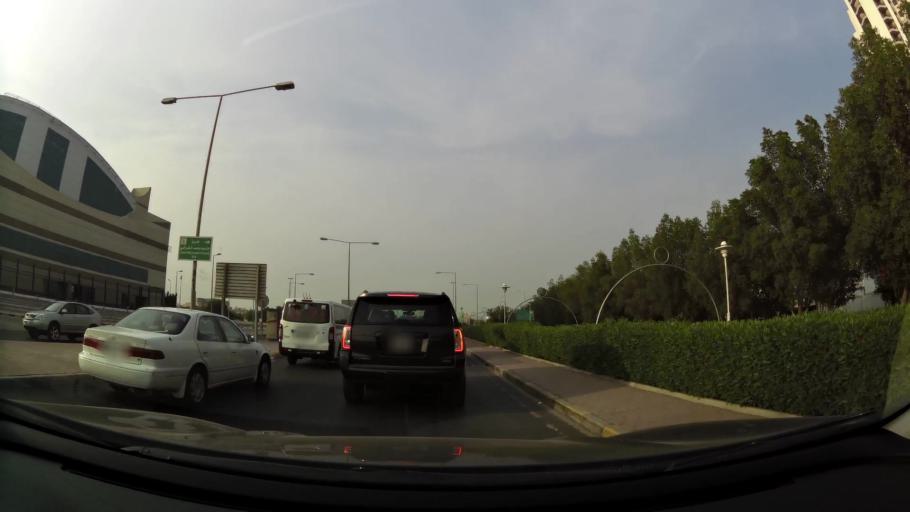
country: KW
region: Mubarak al Kabir
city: Sabah as Salim
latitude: 29.2651
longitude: 48.0765
